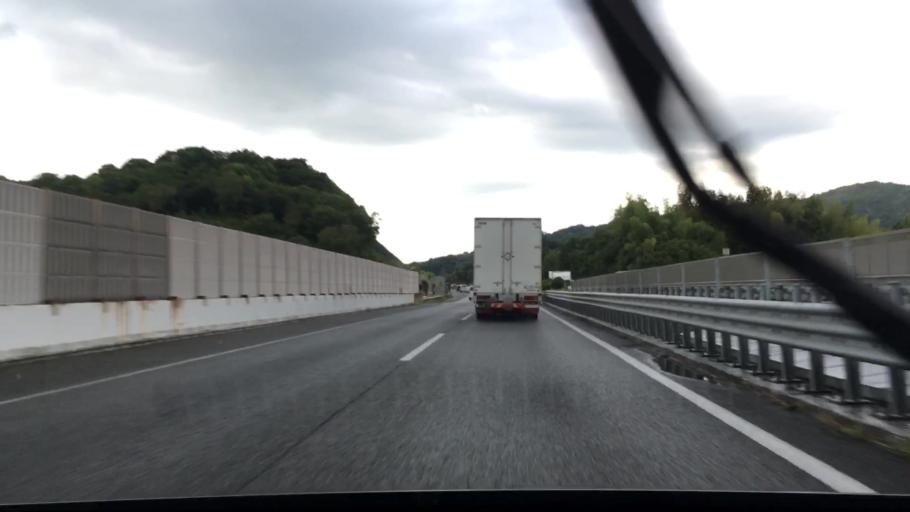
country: JP
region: Fukuoka
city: Koga
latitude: 33.6708
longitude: 130.4819
